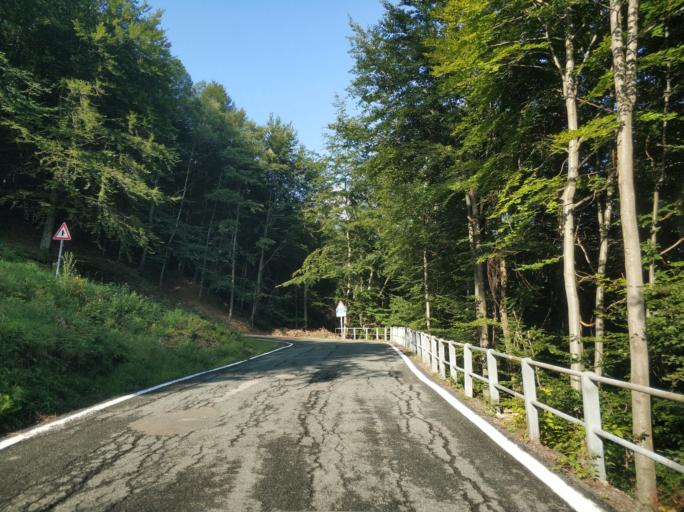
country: IT
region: Piedmont
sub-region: Provincia di Torino
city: Viu
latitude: 45.2246
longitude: 7.3905
